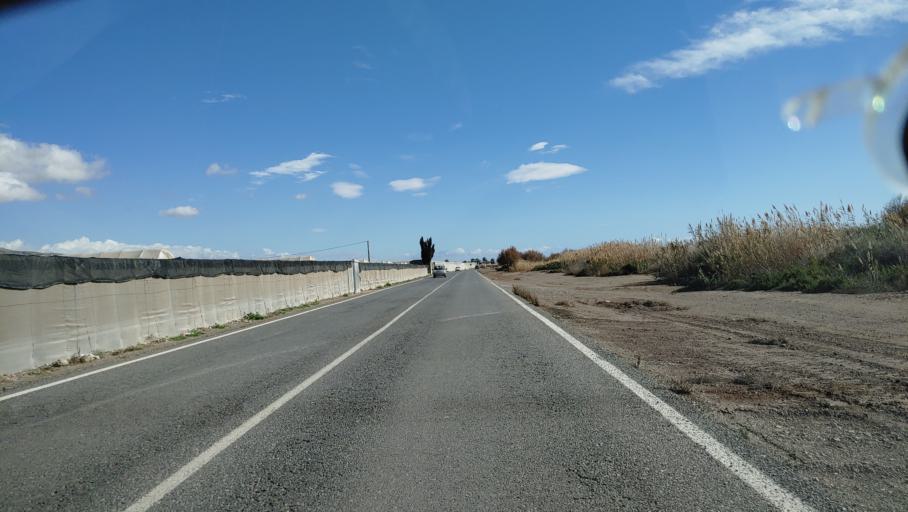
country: ES
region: Andalusia
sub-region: Provincia de Almeria
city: Roquetas de Mar
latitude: 36.7899
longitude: -2.5972
